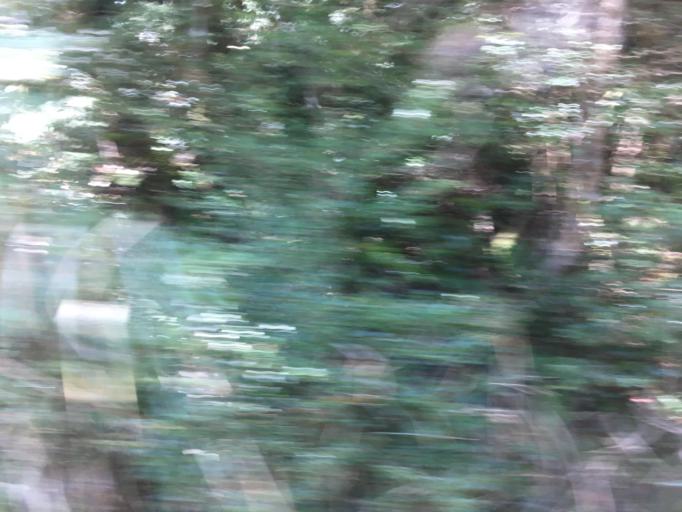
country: TW
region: Taiwan
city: Daxi
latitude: 24.5850
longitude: 121.4121
